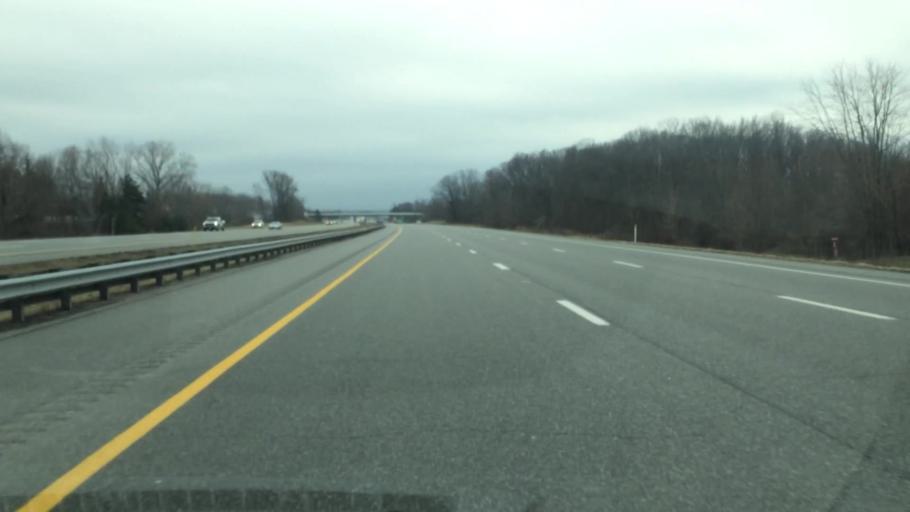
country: US
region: Ohio
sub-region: Cuyahoga County
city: Strongsville
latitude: 41.2817
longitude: -81.8077
